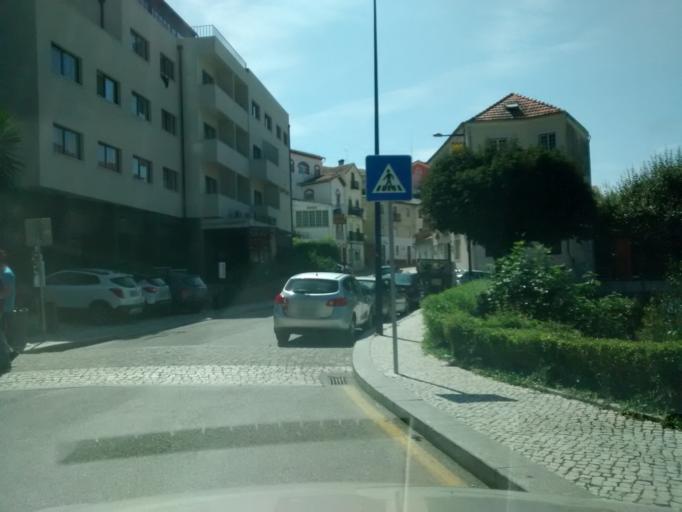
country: PT
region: Aveiro
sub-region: Mealhada
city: Pampilhosa do Botao
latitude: 40.3830
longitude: -8.3760
